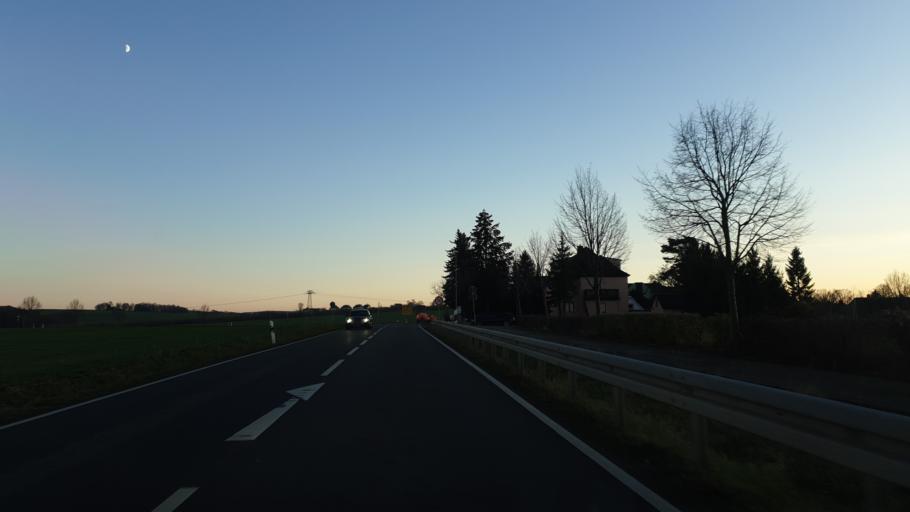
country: DE
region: Saxony
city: Gersdorf
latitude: 50.7617
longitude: 12.7174
